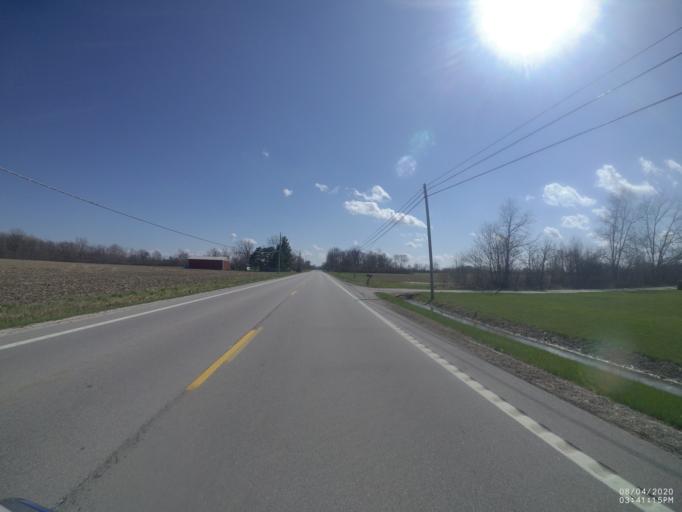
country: US
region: Ohio
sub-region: Sandusky County
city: Stony Prairie
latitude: 41.2637
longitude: -83.2354
